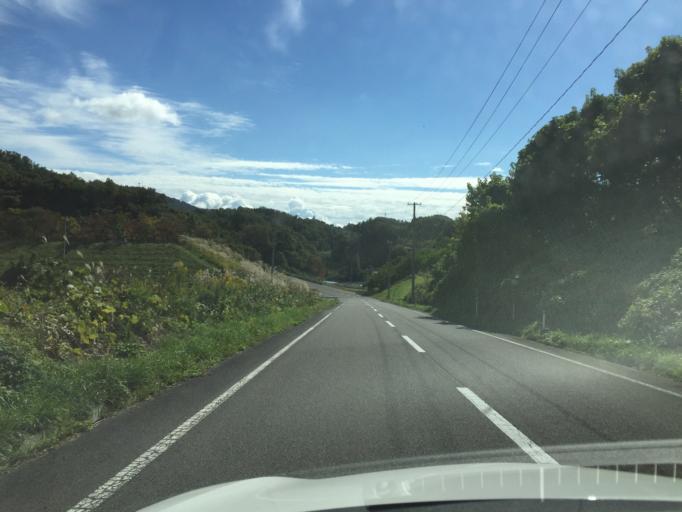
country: JP
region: Fukushima
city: Funehikimachi-funehiki
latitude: 37.4375
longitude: 140.5334
